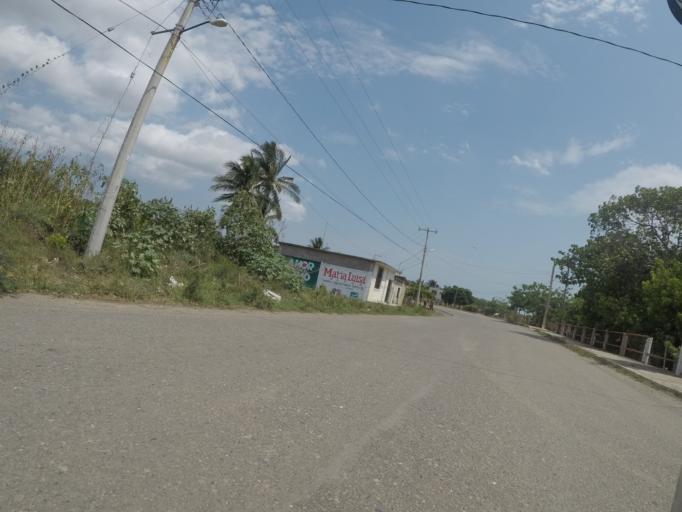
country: MX
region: Oaxaca
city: Union Hidalgo
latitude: 16.4629
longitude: -94.8296
